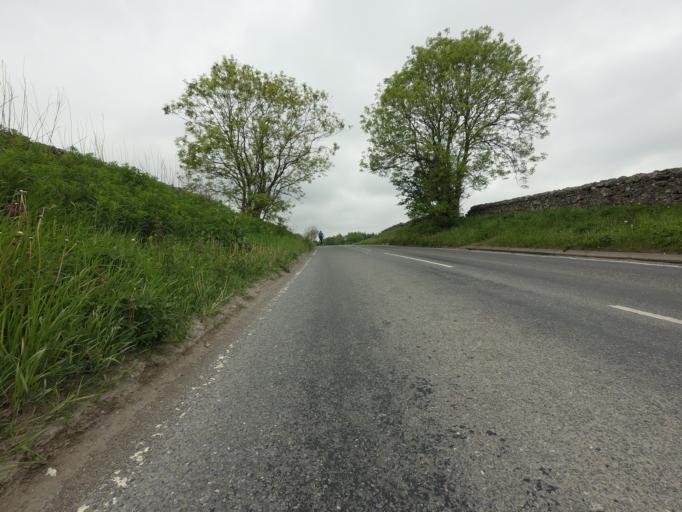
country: GB
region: Scotland
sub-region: Fife
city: Townhill
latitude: 56.1171
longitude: -3.4445
